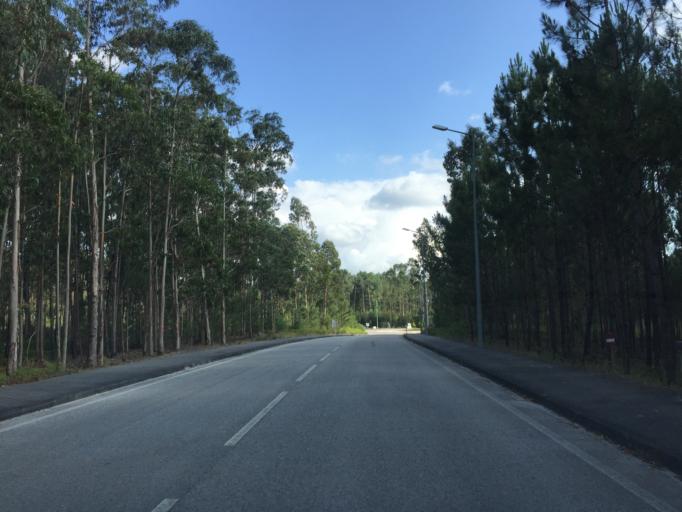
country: PT
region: Leiria
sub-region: Leiria
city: Monte Redondo
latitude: 39.9444
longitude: -8.7985
